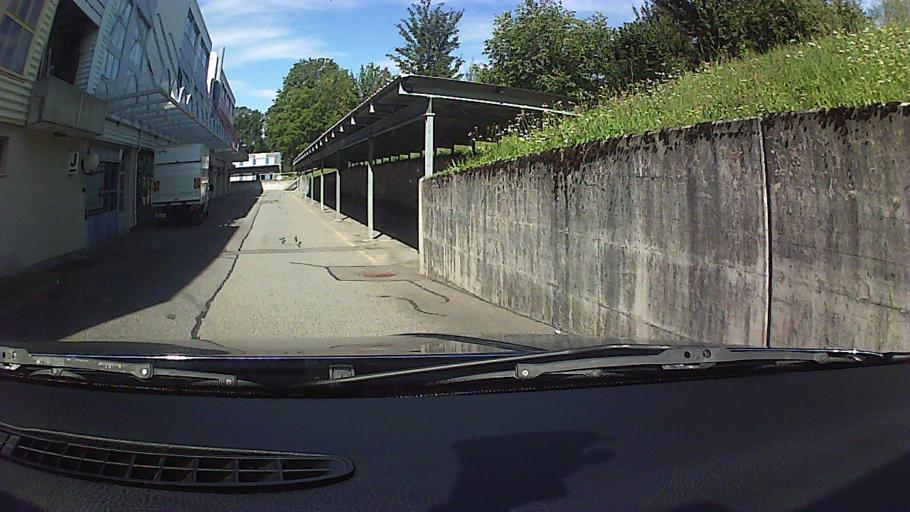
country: CH
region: Fribourg
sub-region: Veveyse District
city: Chatel-Saint-Denis
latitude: 46.5231
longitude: 6.9050
